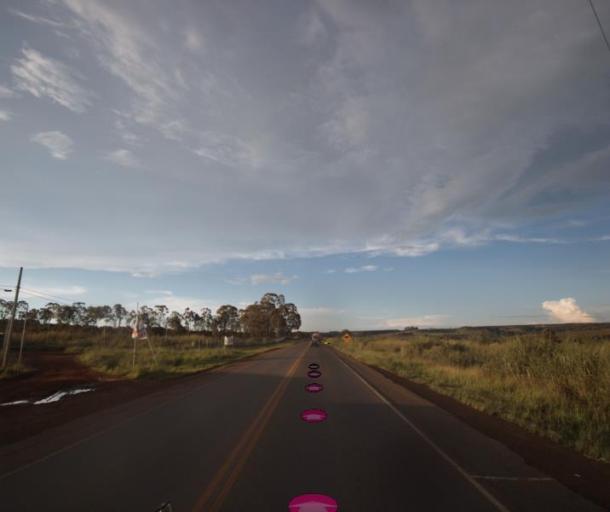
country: BR
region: Goias
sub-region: Anapolis
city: Anapolis
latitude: -16.2618
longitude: -48.9378
